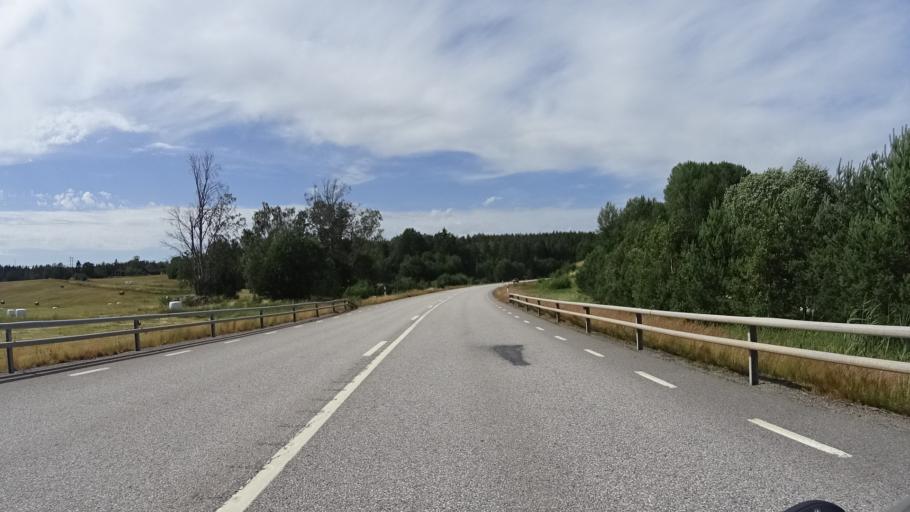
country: SE
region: Kalmar
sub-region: Vasterviks Kommun
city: Overum
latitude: 57.9665
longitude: 16.3411
